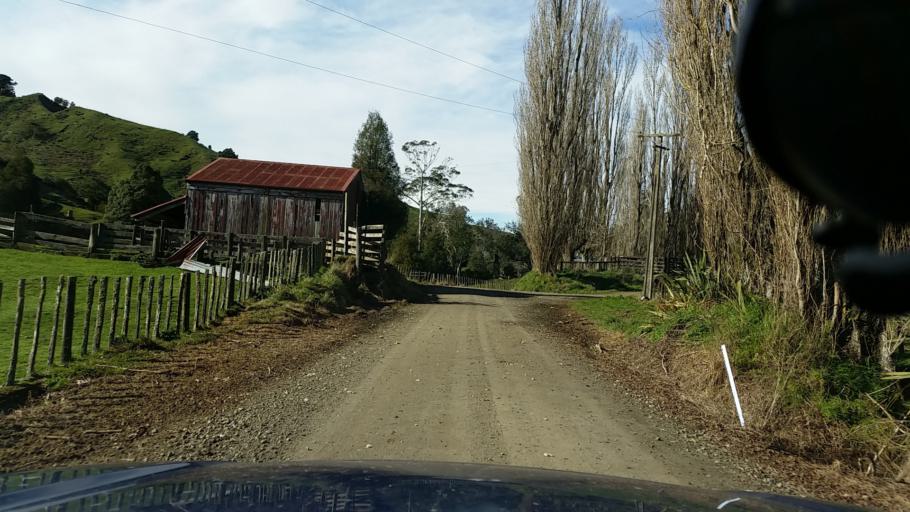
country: NZ
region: Taranaki
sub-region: New Plymouth District
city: Waitara
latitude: -39.0577
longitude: 174.7761
